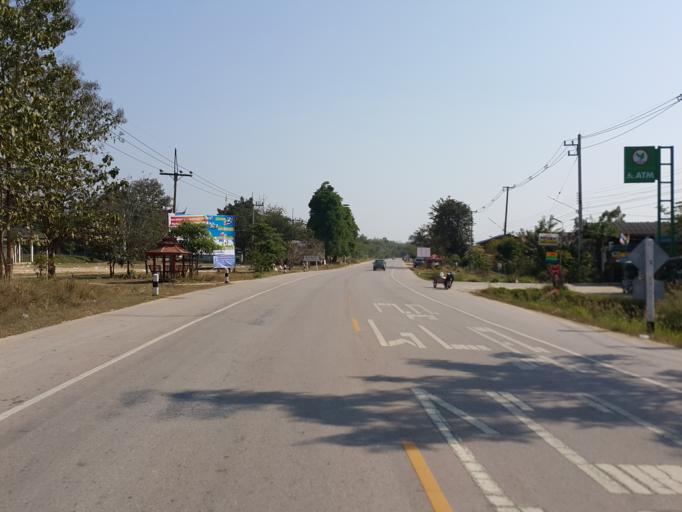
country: TH
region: Lampang
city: Chae Hom
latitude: 18.7484
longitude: 99.5746
